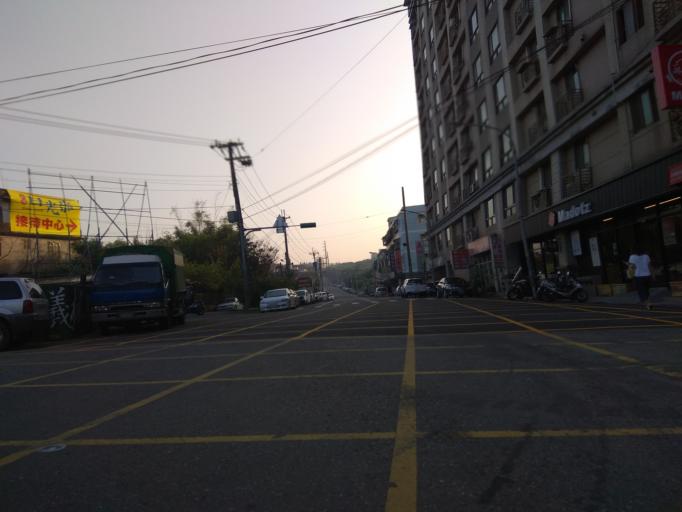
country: TW
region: Taiwan
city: Daxi
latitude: 24.9057
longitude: 121.1774
